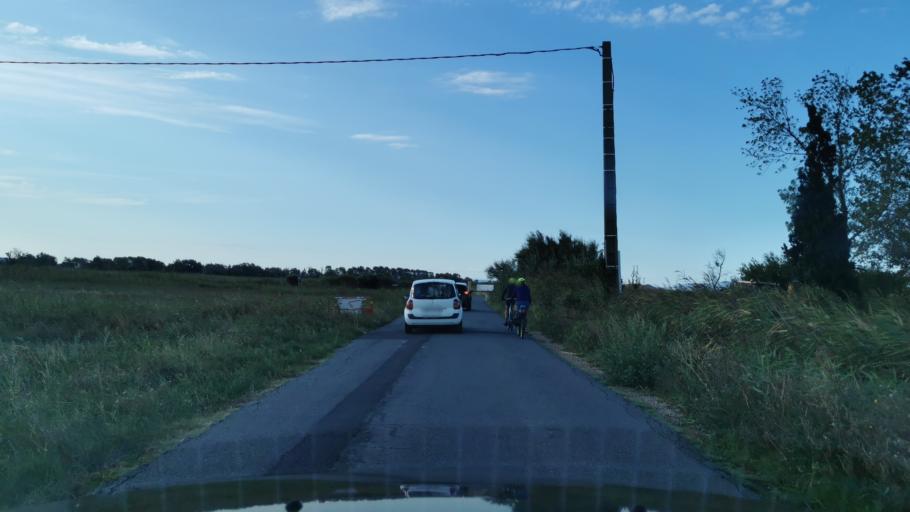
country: FR
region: Languedoc-Roussillon
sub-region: Departement de l'Aude
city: Narbonne
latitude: 43.1314
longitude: 3.0250
